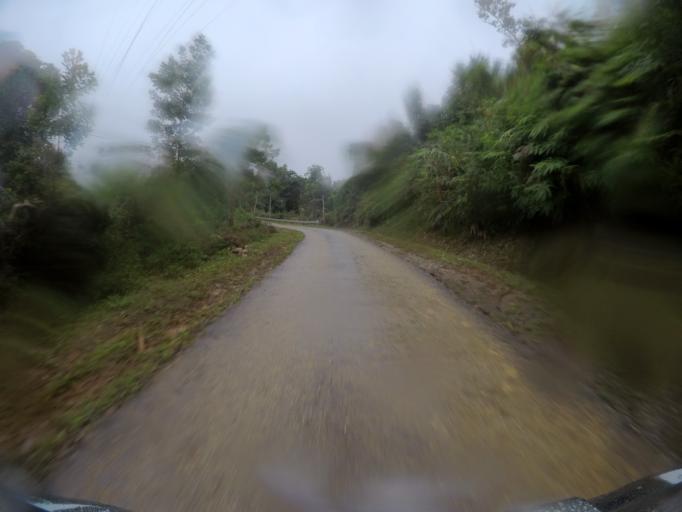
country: LA
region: Xekong
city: Dak Cheung
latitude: 15.5827
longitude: 107.4179
